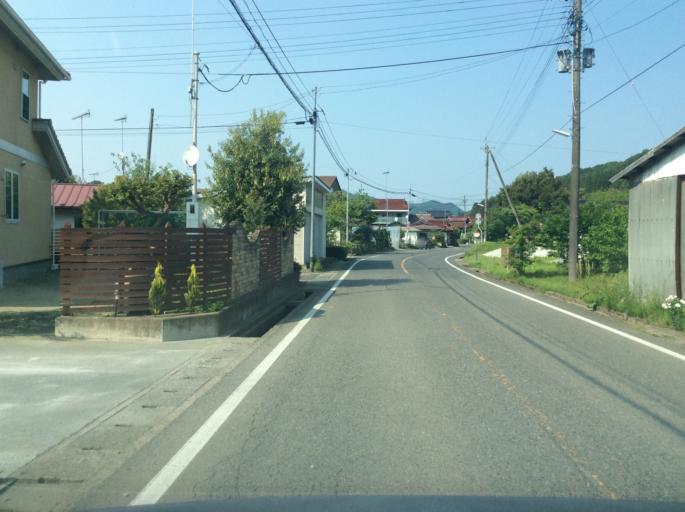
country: JP
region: Tochigi
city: Kuroiso
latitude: 37.0499
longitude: 140.2293
